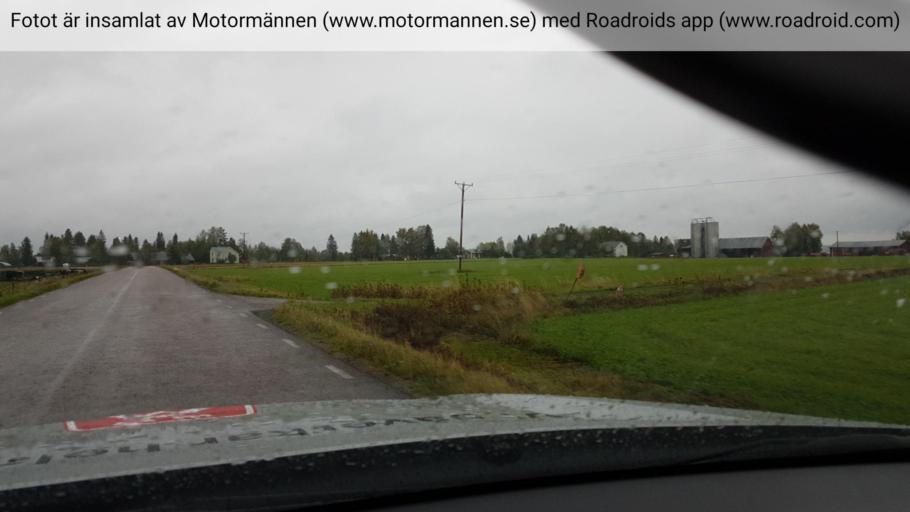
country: SE
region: Norrbotten
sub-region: Lulea Kommun
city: Gammelstad
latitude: 65.7584
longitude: 22.0981
